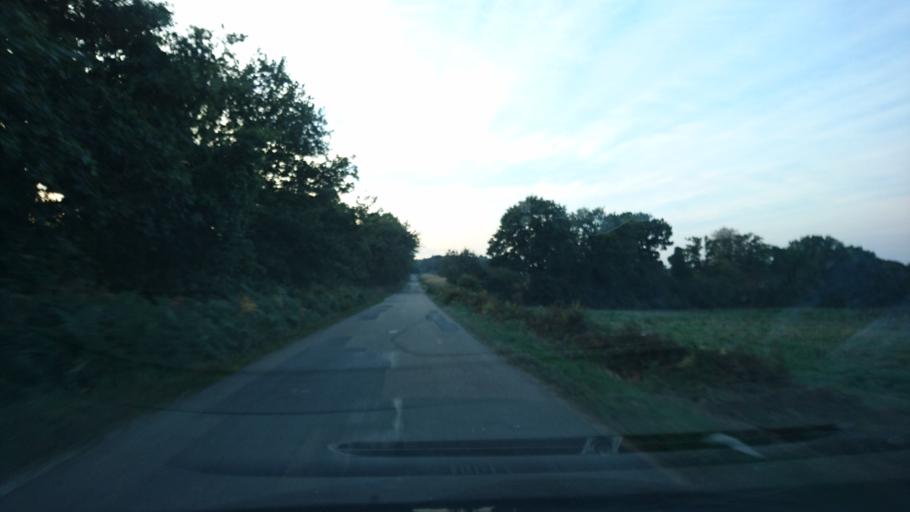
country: FR
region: Brittany
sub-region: Departement d'Ille-et-Vilaine
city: Maure-de-Bretagne
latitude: 47.8596
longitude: -2.0180
